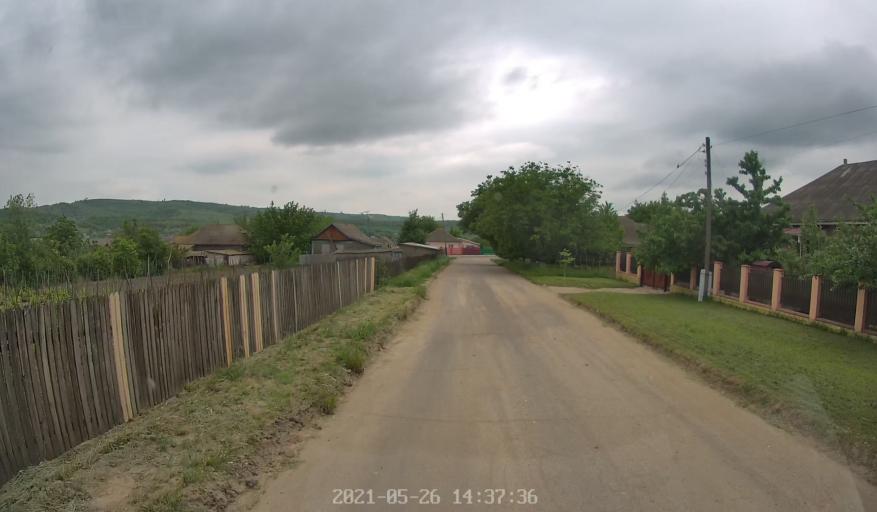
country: MD
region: Hincesti
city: Dancu
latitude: 46.6742
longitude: 28.3305
